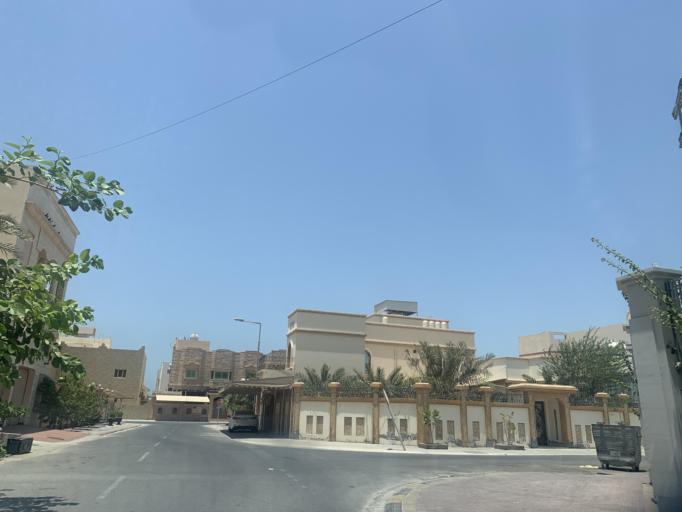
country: BH
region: Muharraq
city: Al Muharraq
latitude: 26.2854
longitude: 50.6199
